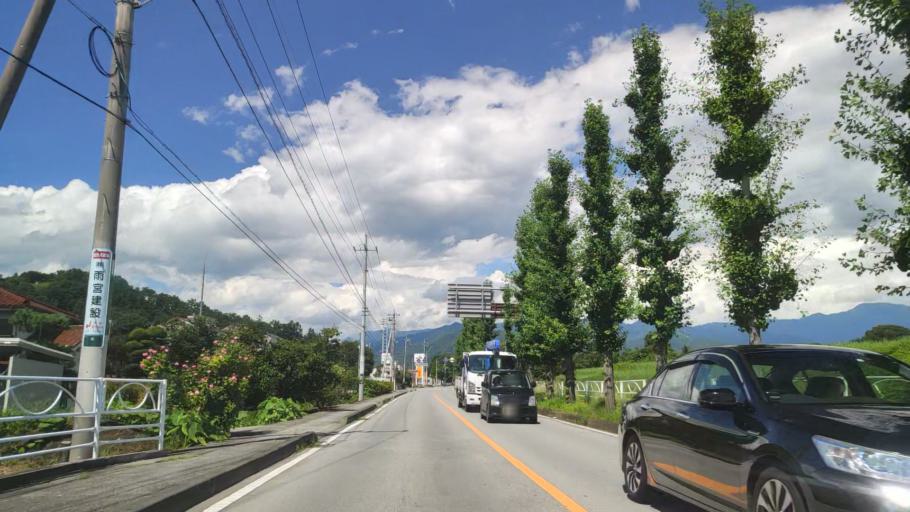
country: JP
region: Yamanashi
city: Enzan
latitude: 35.7040
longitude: 138.6932
